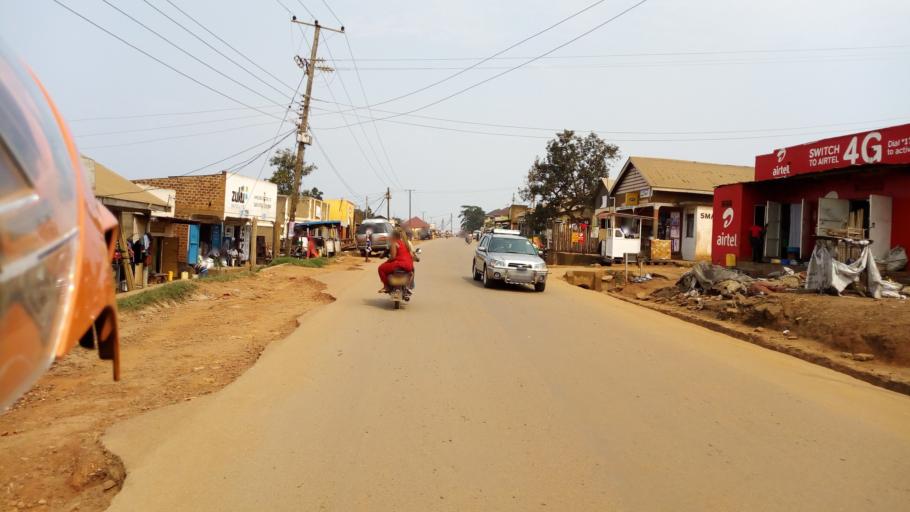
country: UG
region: Central Region
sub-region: Wakiso District
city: Kireka
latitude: 0.3144
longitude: 32.6511
